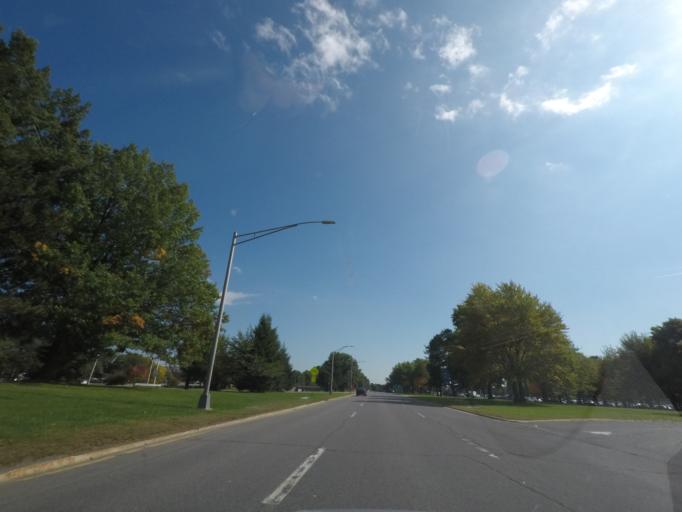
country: US
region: New York
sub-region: Albany County
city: Roessleville
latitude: 42.6835
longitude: -73.8106
